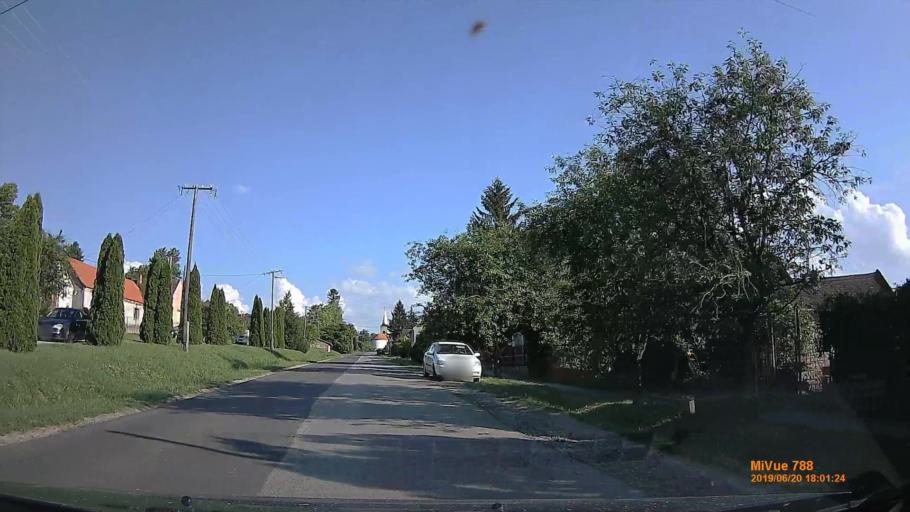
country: HU
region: Baranya
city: Buekkoesd
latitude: 46.0833
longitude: 17.9898
